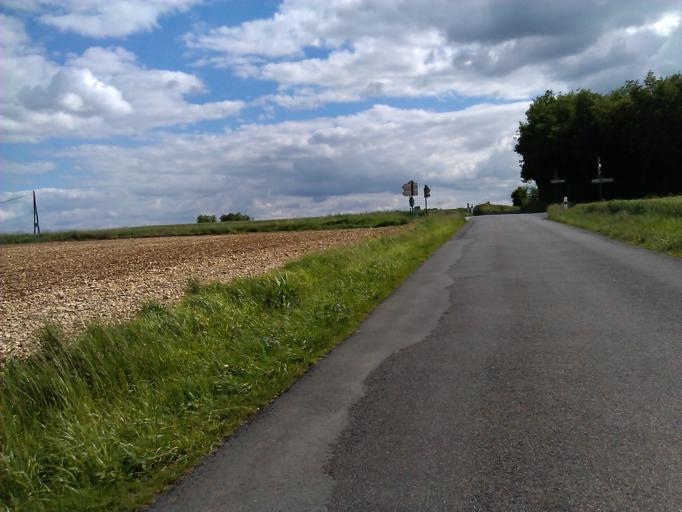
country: FR
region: Poitou-Charentes
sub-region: Departement de la Charente
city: Mansle
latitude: 45.9009
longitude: 0.2130
